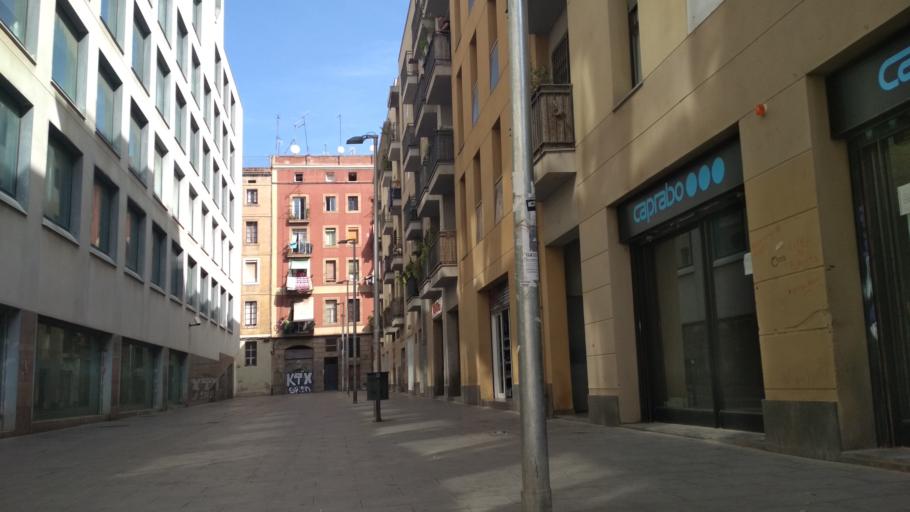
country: ES
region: Catalonia
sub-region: Provincia de Barcelona
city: Ciutat Vella
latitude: 41.3789
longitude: 2.1704
